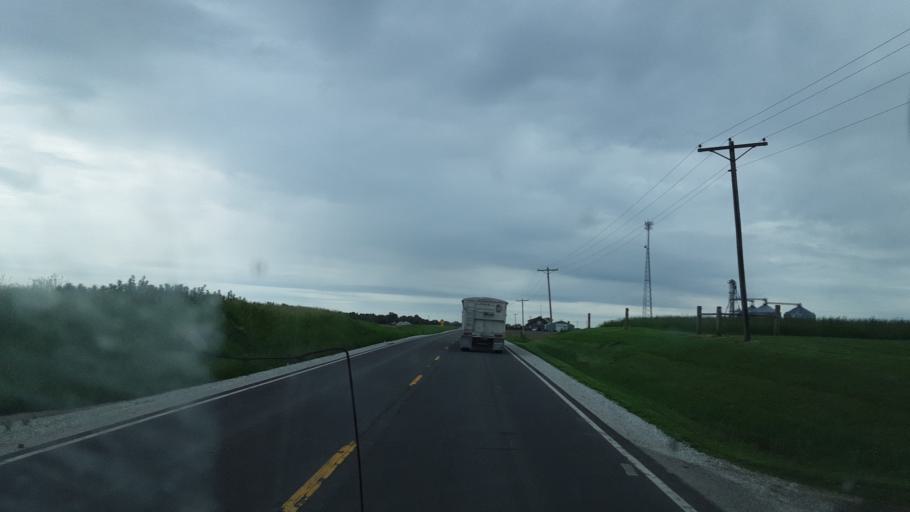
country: US
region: Illinois
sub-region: Fulton County
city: Lewistown
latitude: 40.3095
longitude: -90.1908
